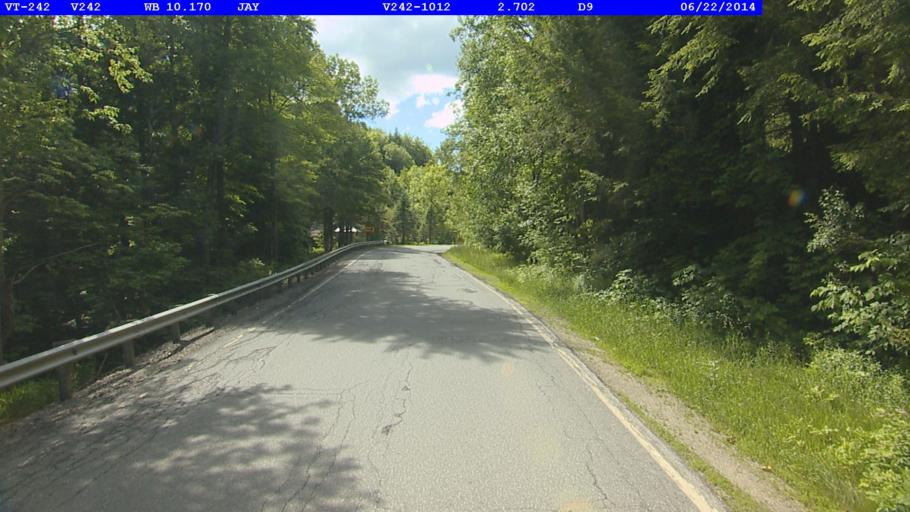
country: US
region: Vermont
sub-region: Franklin County
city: Richford
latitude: 44.9398
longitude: -72.4605
